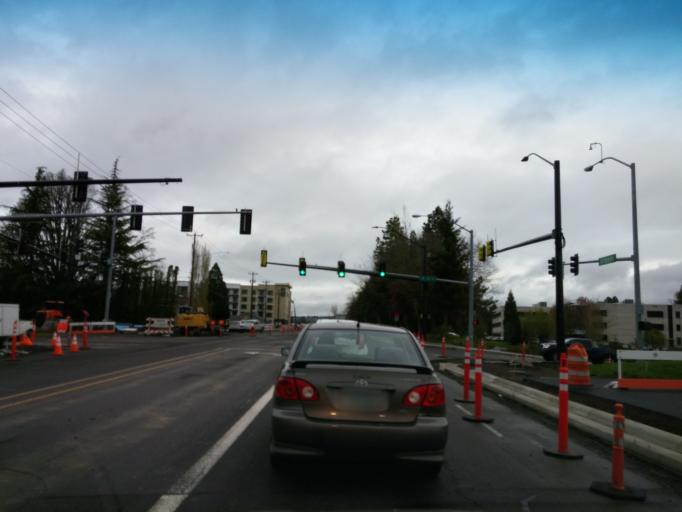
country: US
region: Oregon
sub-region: Washington County
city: Aloha
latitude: 45.5094
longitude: -122.8401
